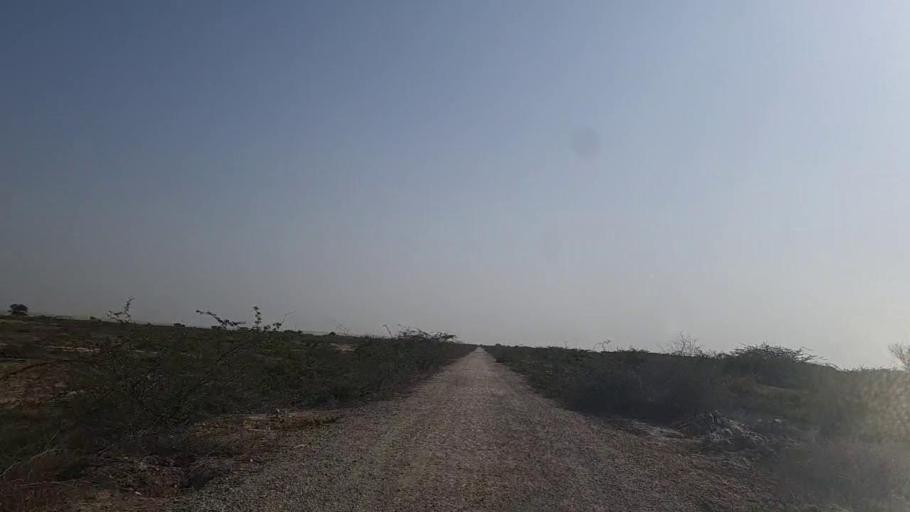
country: PK
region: Sindh
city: Naukot
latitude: 24.6016
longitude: 69.2647
